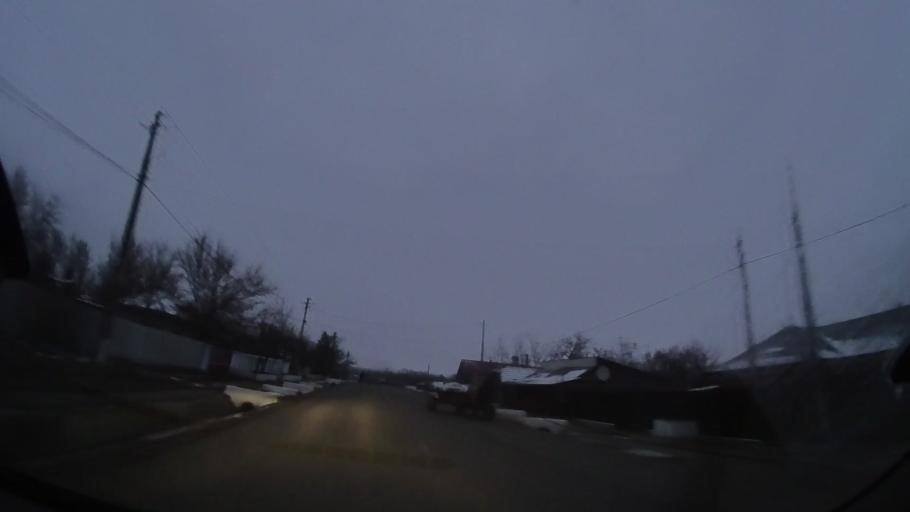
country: RO
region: Vaslui
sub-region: Comuna Dimitrie Cantemir
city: Dimitrie Cantemir
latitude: 46.4610
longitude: 28.0283
